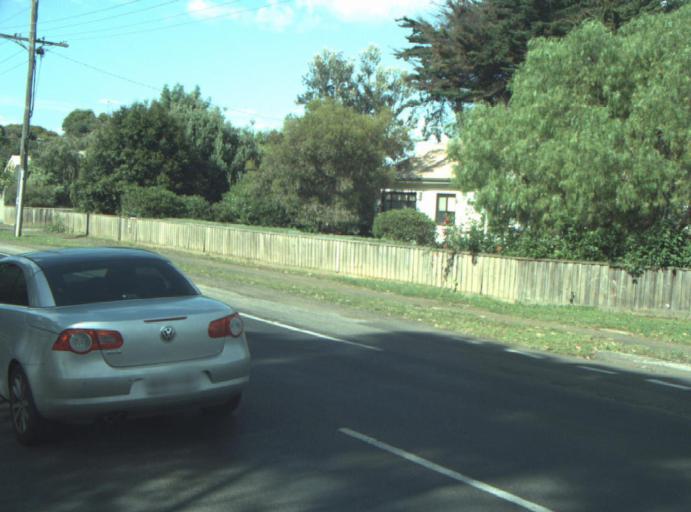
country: AU
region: Victoria
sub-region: Greater Geelong
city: Leopold
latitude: -38.2800
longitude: 144.5259
